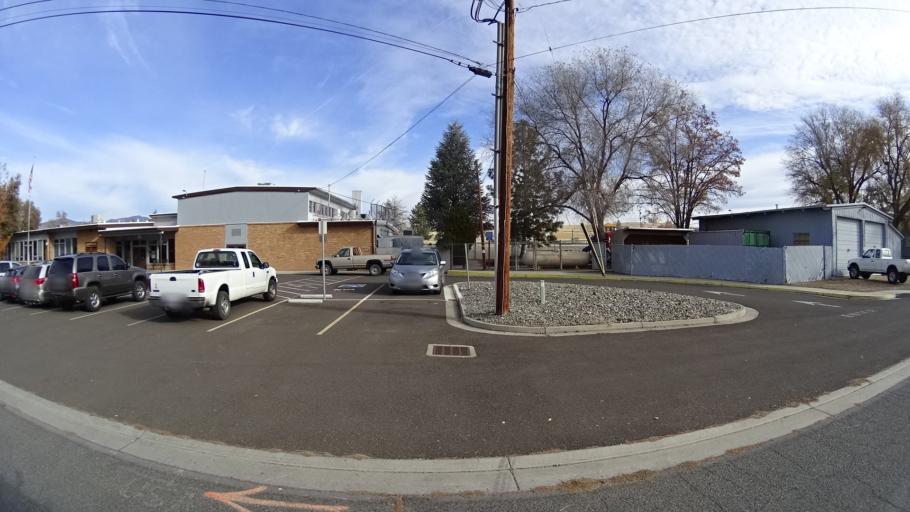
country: US
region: California
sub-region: Siskiyou County
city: Montague
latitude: 41.7273
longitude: -122.5215
